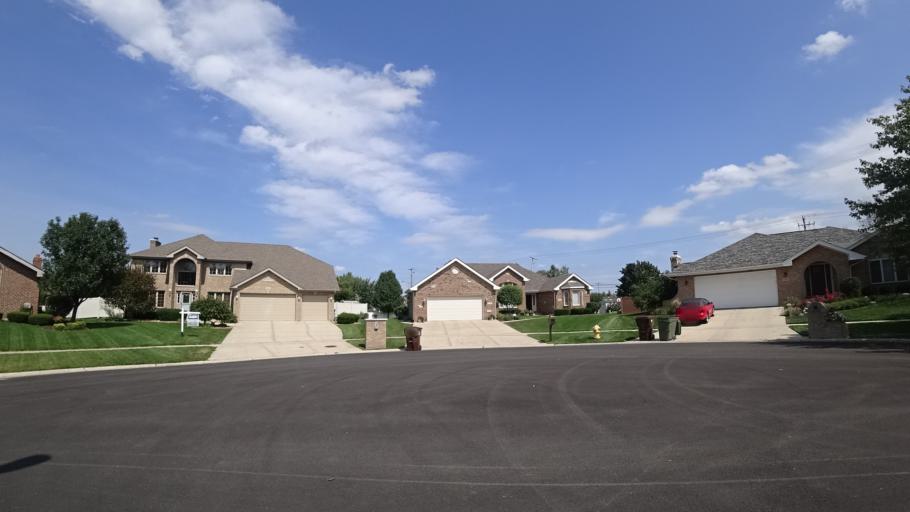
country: US
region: Illinois
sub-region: Cook County
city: Tinley Park
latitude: 41.5722
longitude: -87.8136
